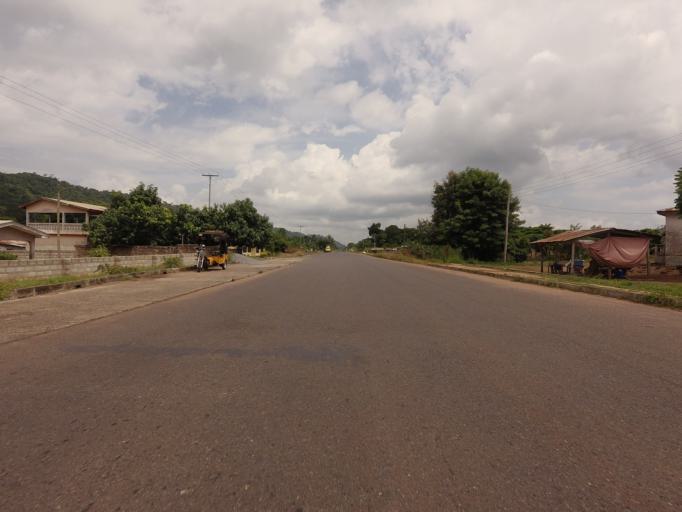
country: GH
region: Volta
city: Ho
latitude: 6.4999
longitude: 0.2049
